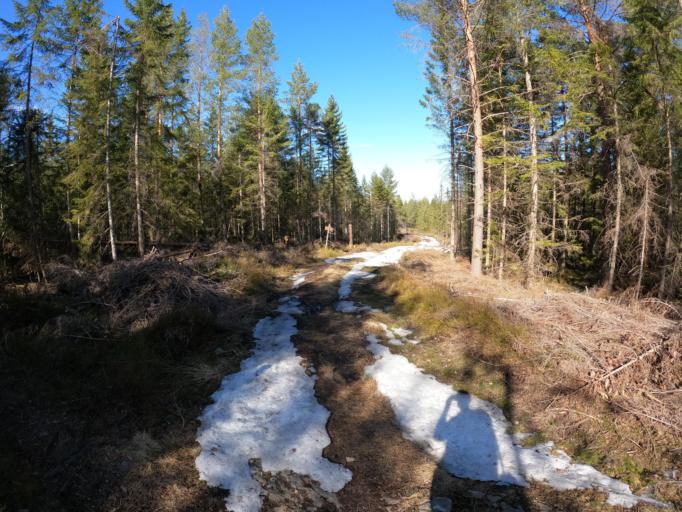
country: NO
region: Akershus
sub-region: Gjerdrum
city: Ask
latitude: 60.0587
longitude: 10.9613
